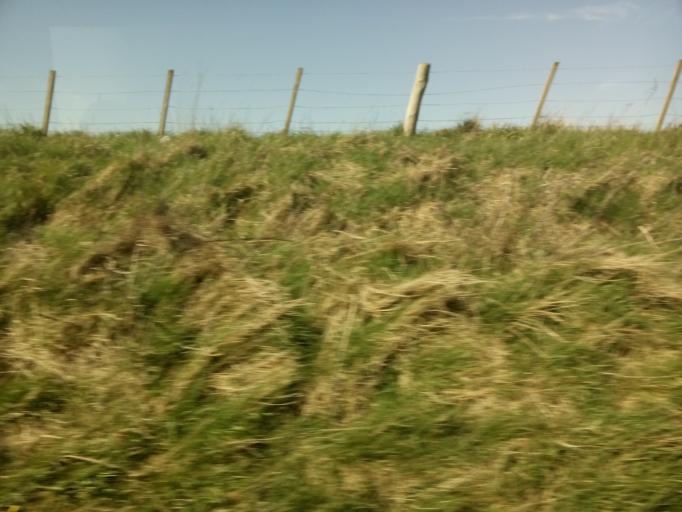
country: GB
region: Scotland
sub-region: East Lothian
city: Musselburgh
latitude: 55.9408
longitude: -3.0869
